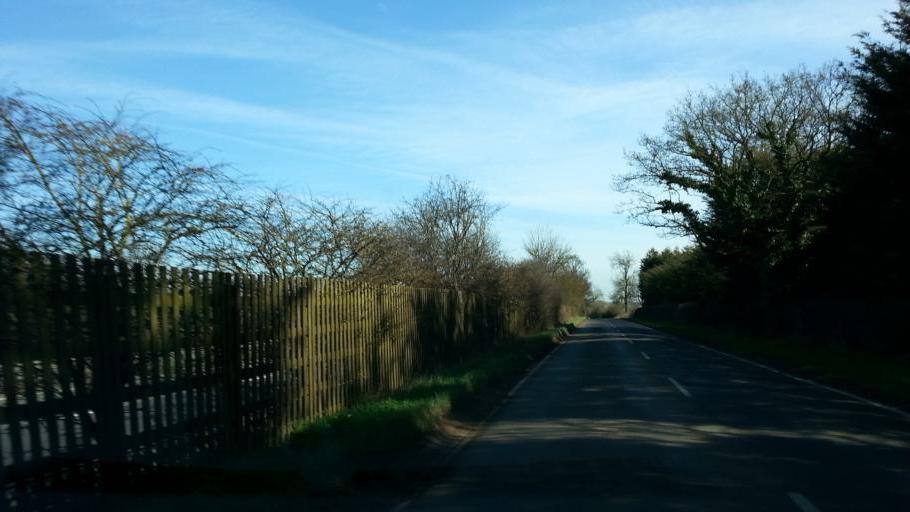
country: GB
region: England
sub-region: Northamptonshire
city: Rothwell
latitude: 52.4104
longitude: -0.8321
